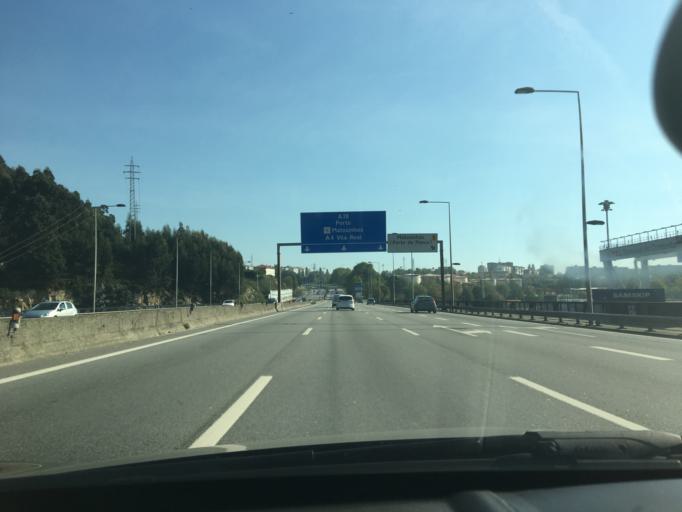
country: PT
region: Porto
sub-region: Matosinhos
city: Matosinhos
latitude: 41.1947
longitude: -8.6824
